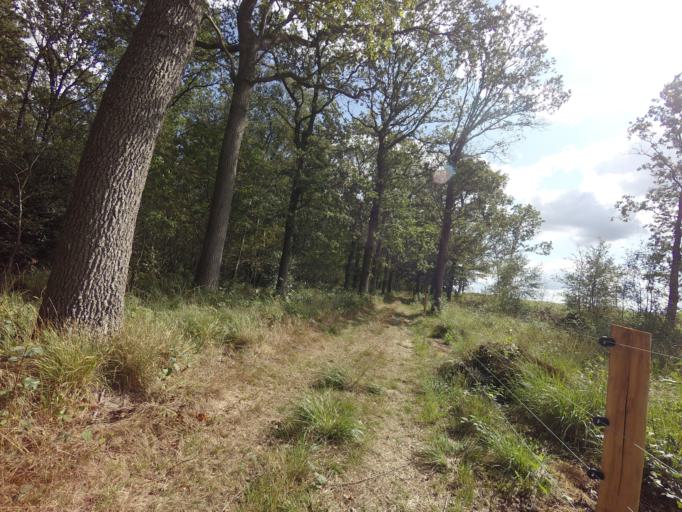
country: NL
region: Friesland
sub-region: Gemeente Weststellingwerf
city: Noordwolde
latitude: 52.9479
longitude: 6.1936
